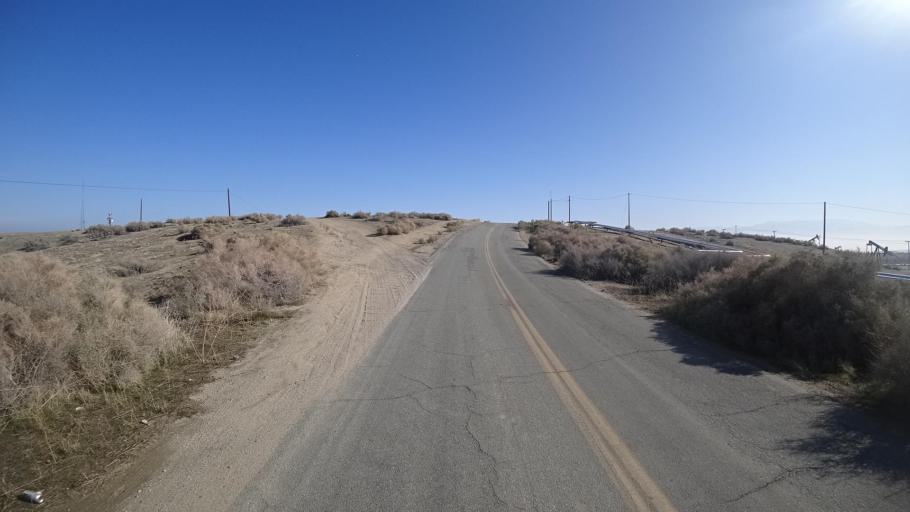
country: US
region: California
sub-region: Kern County
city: South Taft
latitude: 35.1148
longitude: -119.4623
